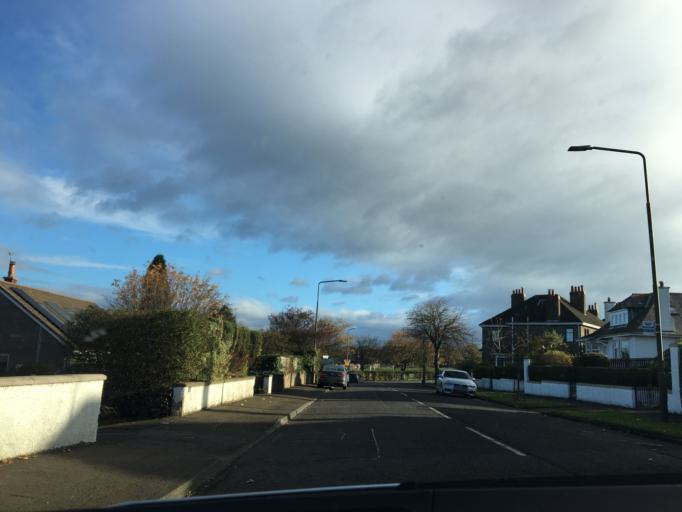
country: GB
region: Scotland
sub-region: East Lothian
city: North Berwick
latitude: 56.0553
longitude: -2.7113
